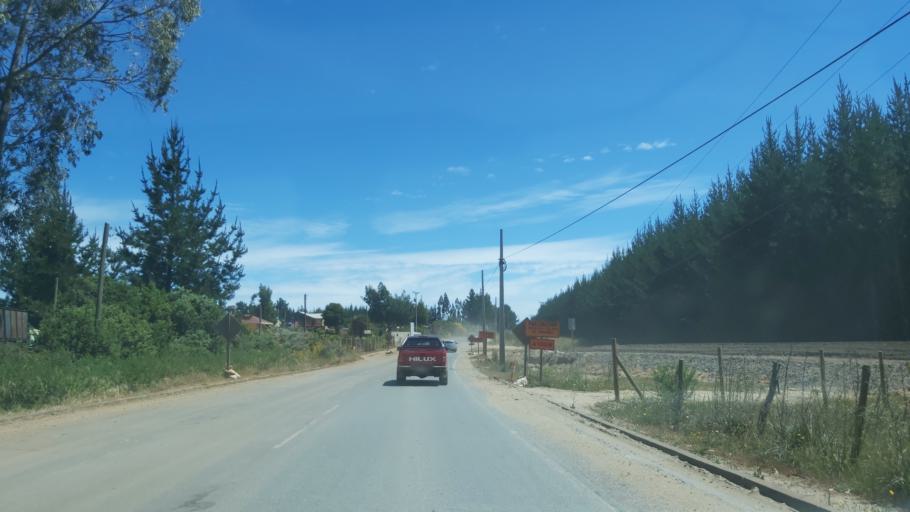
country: CL
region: Maule
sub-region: Provincia de Talca
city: Constitucion
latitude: -35.3914
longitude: -72.4248
